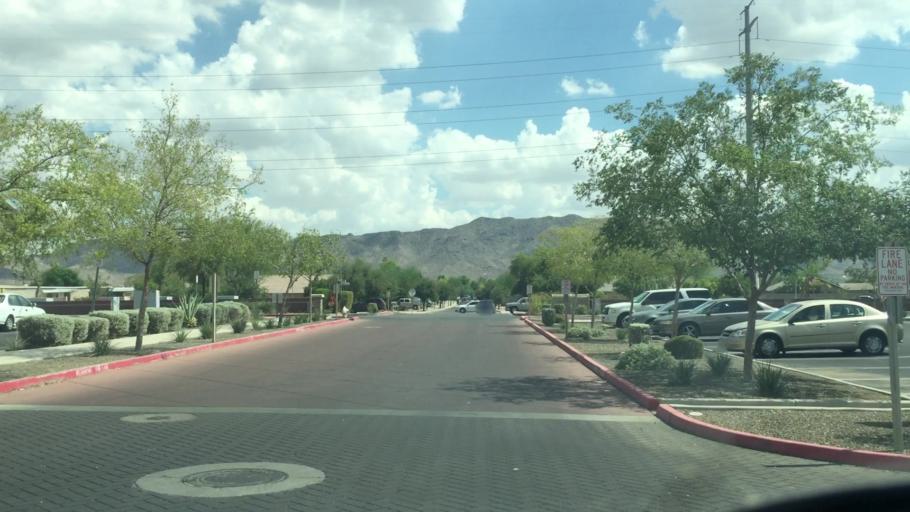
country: US
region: Arizona
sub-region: Maricopa County
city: Laveen
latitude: 33.3787
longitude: -112.1029
